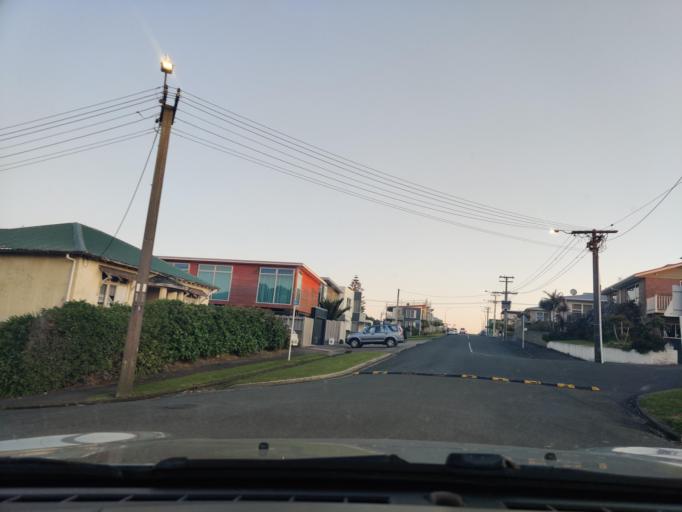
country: NZ
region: Taranaki
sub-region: New Plymouth District
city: New Plymouth
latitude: -39.0506
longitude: 174.0848
